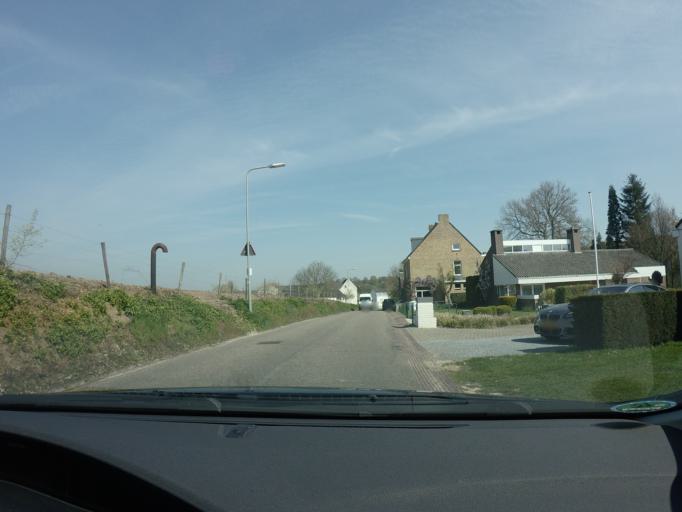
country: NL
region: Limburg
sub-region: Valkenburg aan de Geul
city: Berg
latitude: 50.8434
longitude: 5.7632
